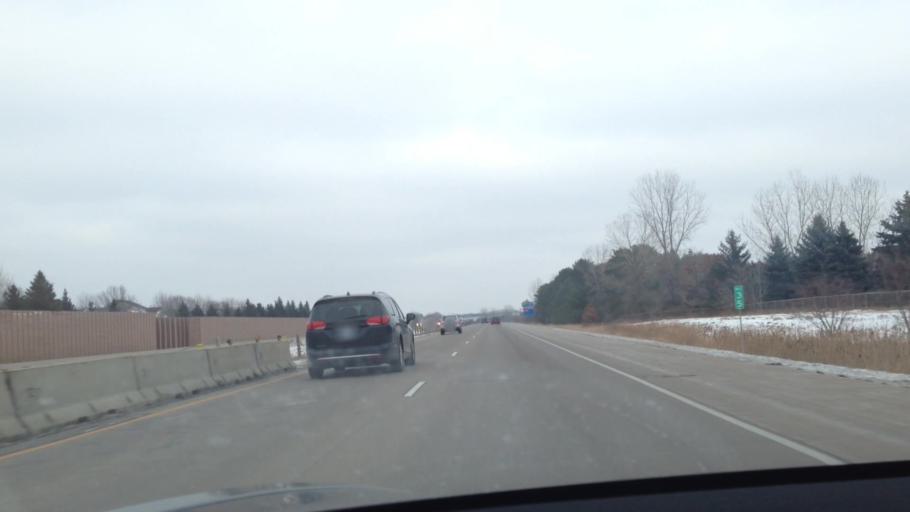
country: US
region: Minnesota
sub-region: Anoka County
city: Circle Pines
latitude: 45.1691
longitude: -93.1386
